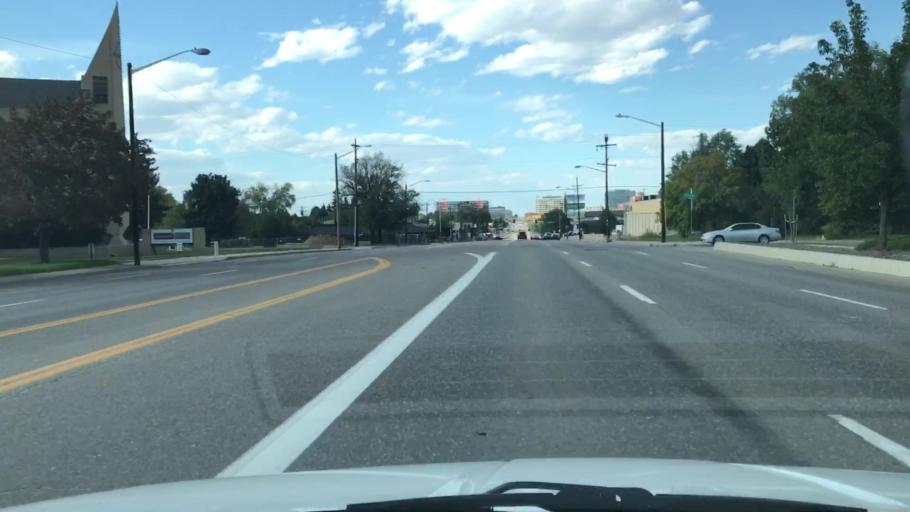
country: US
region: Colorado
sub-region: Arapahoe County
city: Cherry Hills Village
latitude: 39.6630
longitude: -104.9407
